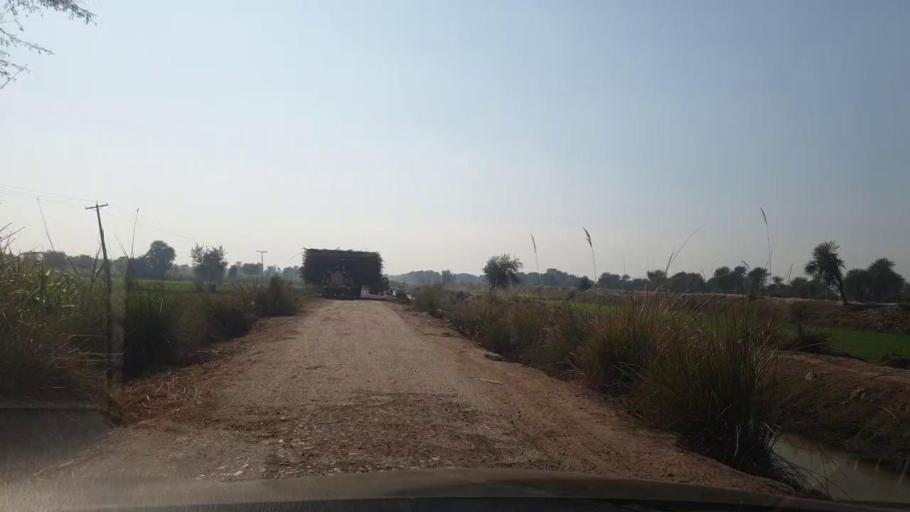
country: PK
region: Sindh
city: Ubauro
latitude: 28.1452
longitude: 69.6886
